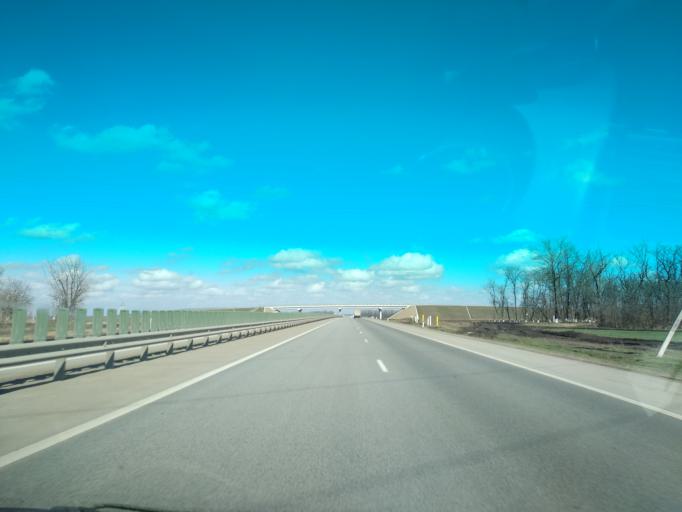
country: RU
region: Krasnodarskiy
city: Korenovsk
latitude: 45.5033
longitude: 39.4295
